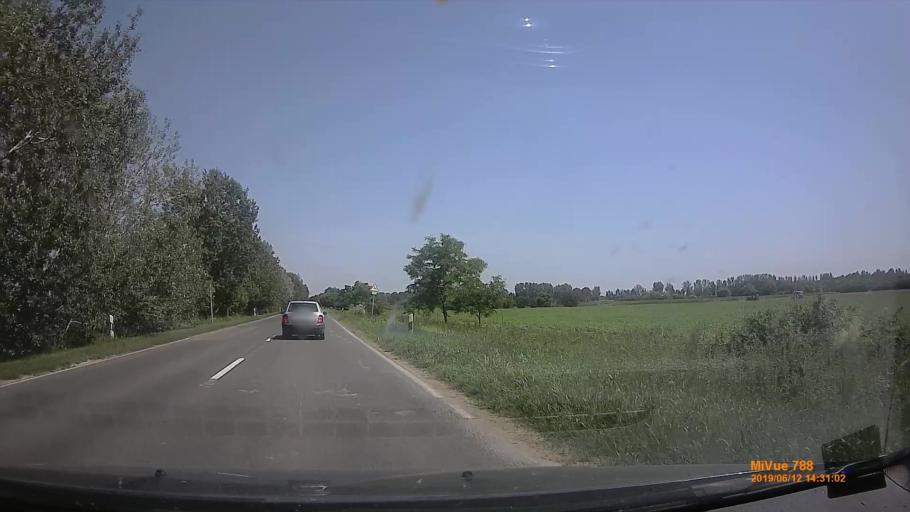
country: HU
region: Csongrad
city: Kiszombor
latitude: 46.1970
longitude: 20.4006
